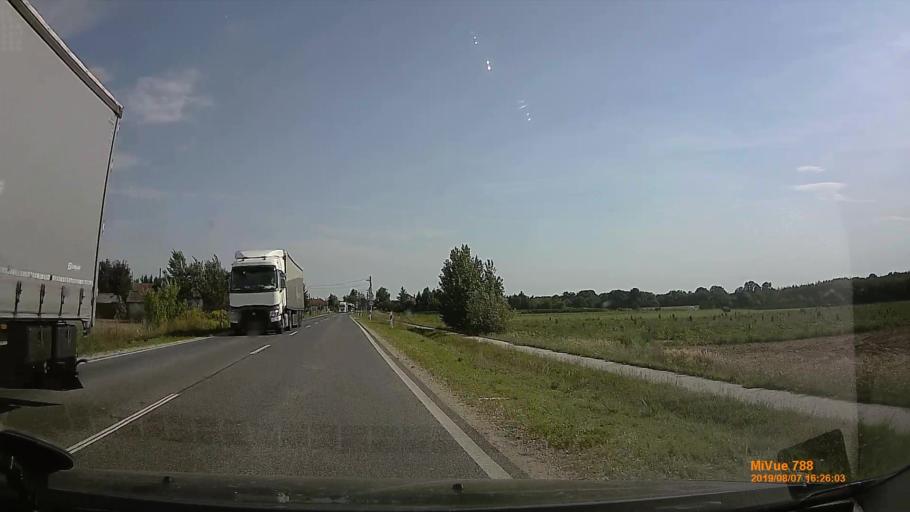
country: HU
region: Zala
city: Lenti
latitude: 46.7140
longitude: 16.5514
